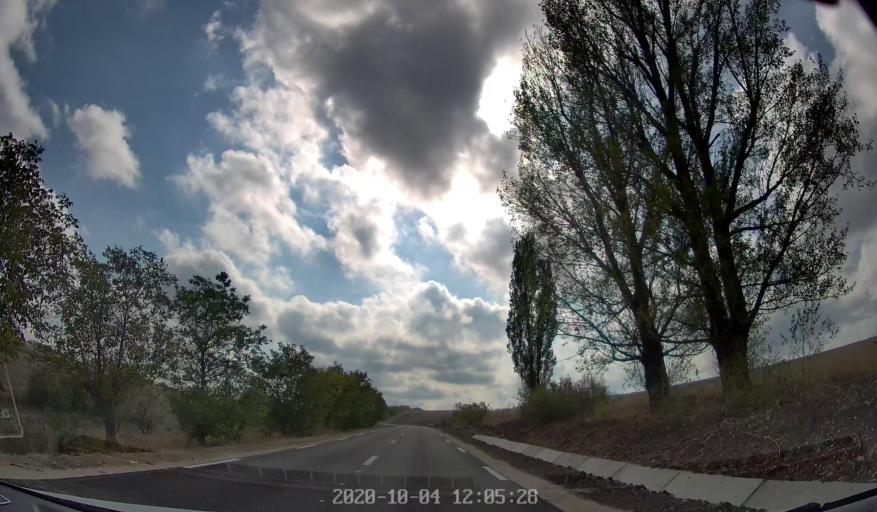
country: MD
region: Rezina
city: Saharna
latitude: 47.5938
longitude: 28.9504
